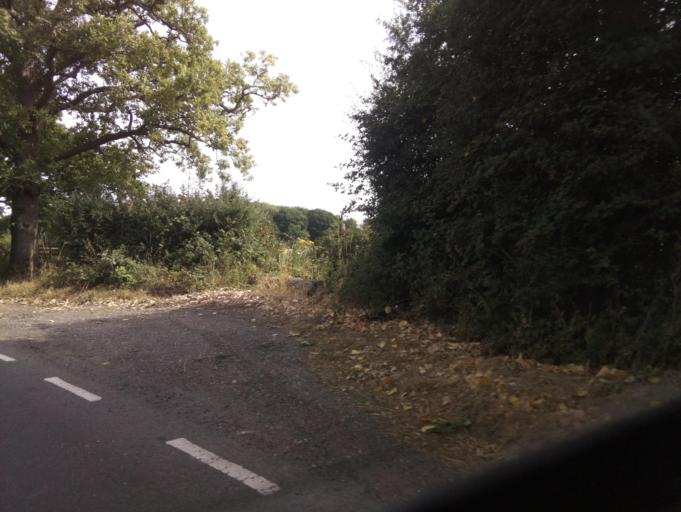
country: GB
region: England
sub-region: Surrey
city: Godstone
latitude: 51.1962
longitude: -0.0646
